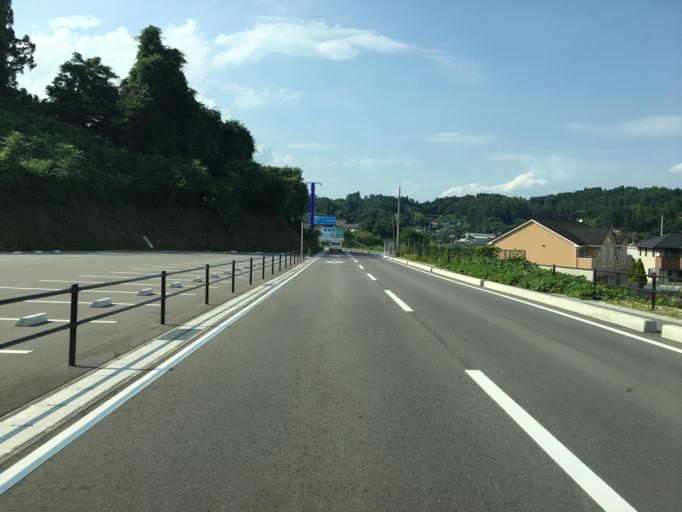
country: JP
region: Fukushima
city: Nihommatsu
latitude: 37.5883
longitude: 140.4451
